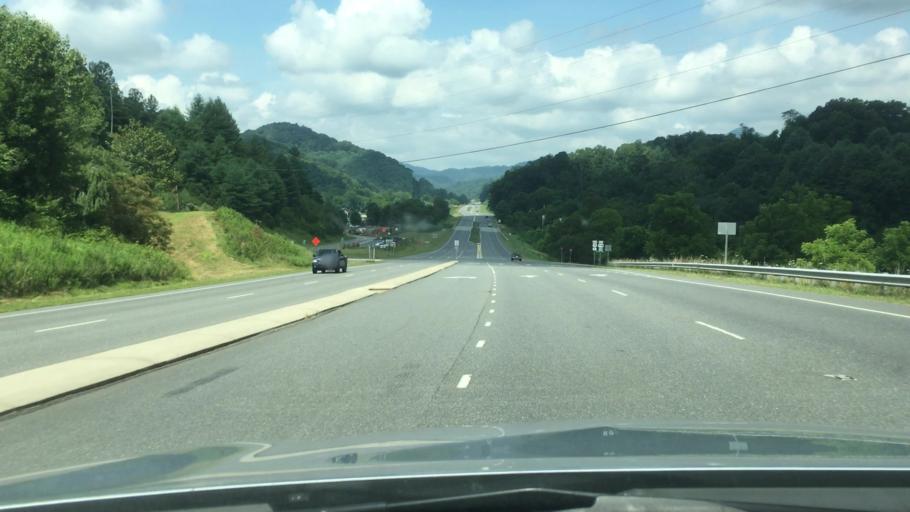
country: US
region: North Carolina
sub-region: Yancey County
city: Burnsville
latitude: 35.9133
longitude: -82.3957
